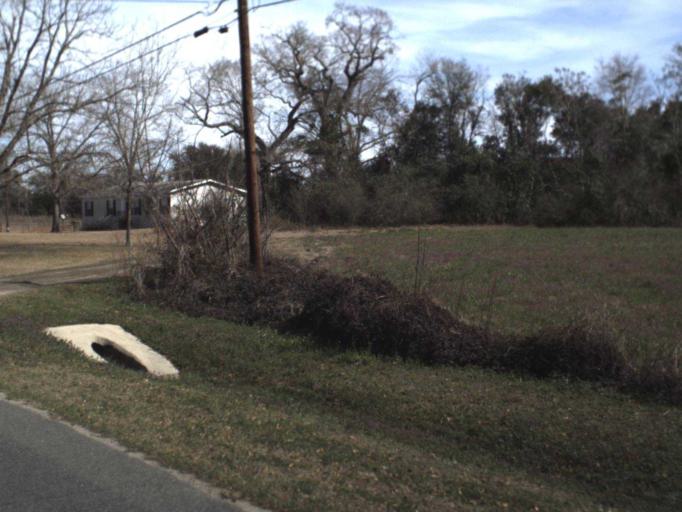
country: US
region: Florida
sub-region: Jackson County
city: Graceville
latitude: 30.9717
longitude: -85.5044
